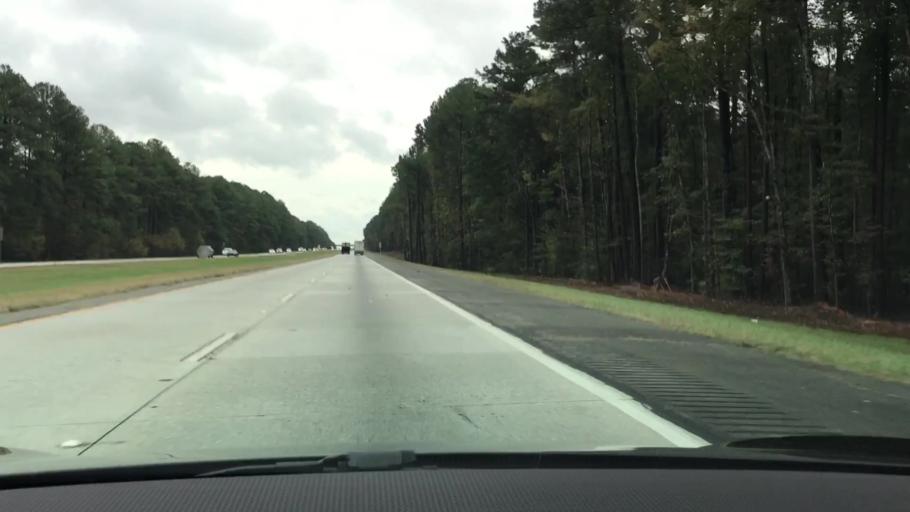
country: US
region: Georgia
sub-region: Taliaferro County
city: Crawfordville
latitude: 33.5166
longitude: -82.8588
